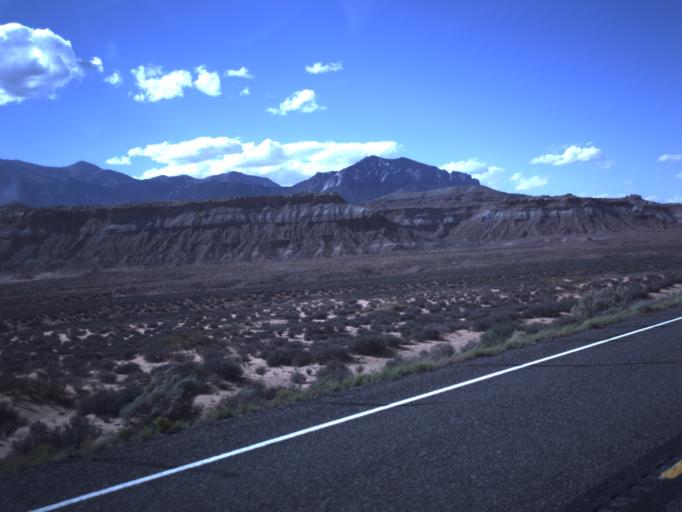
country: US
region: Utah
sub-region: Wayne County
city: Loa
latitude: 38.0854
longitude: -110.6150
